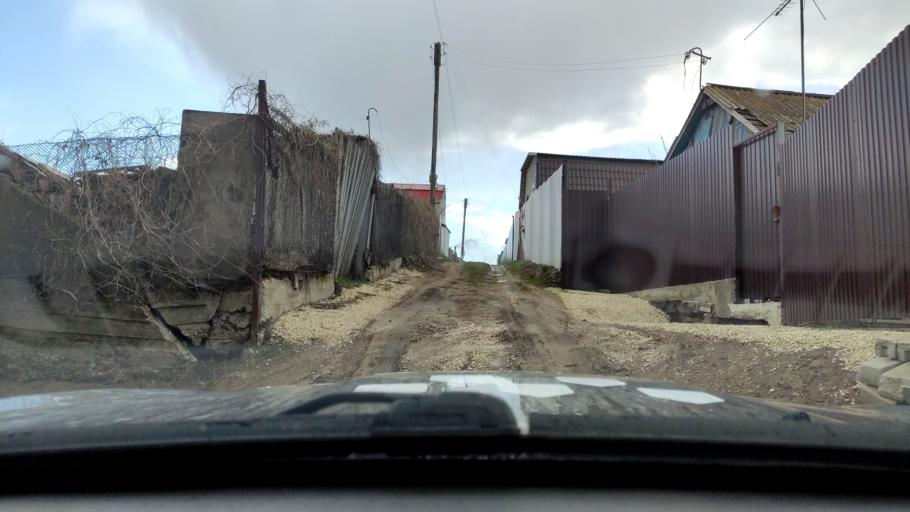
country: RU
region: Samara
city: Zhigulevsk
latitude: 53.4959
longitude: 49.4955
